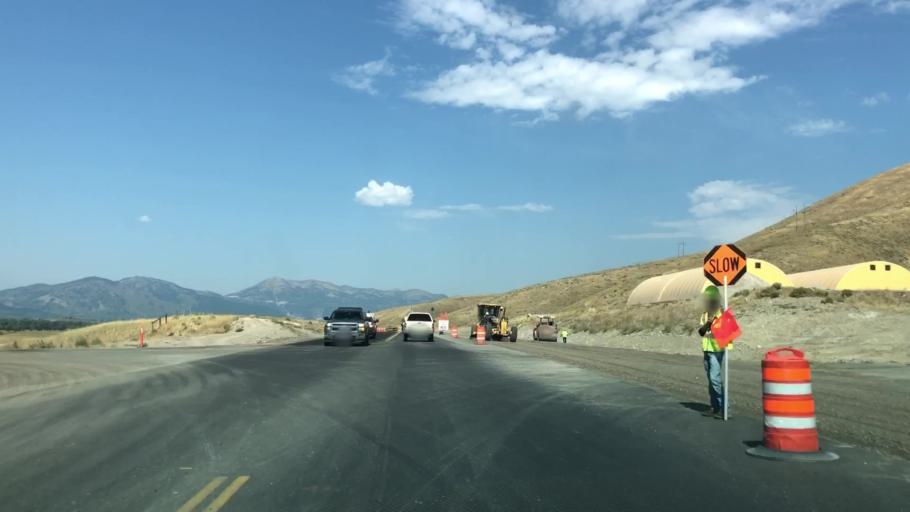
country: US
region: Wyoming
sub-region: Teton County
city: South Park
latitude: 43.4010
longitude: -110.7536
